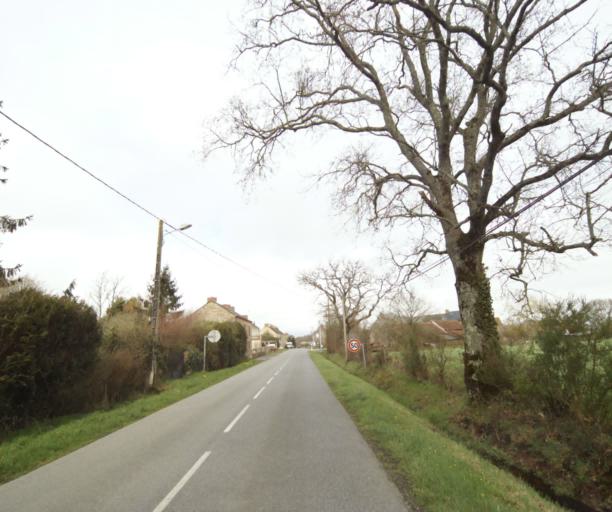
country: FR
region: Pays de la Loire
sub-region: Departement de la Loire-Atlantique
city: Bouvron
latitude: 47.4241
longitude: -1.8985
